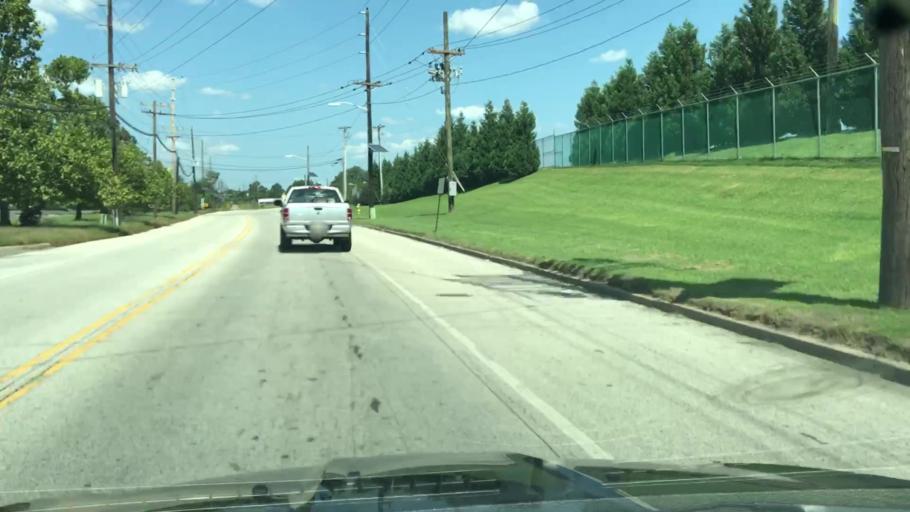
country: US
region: New Jersey
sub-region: Burlington County
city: Palmyra
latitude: 39.9910
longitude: -75.0391
